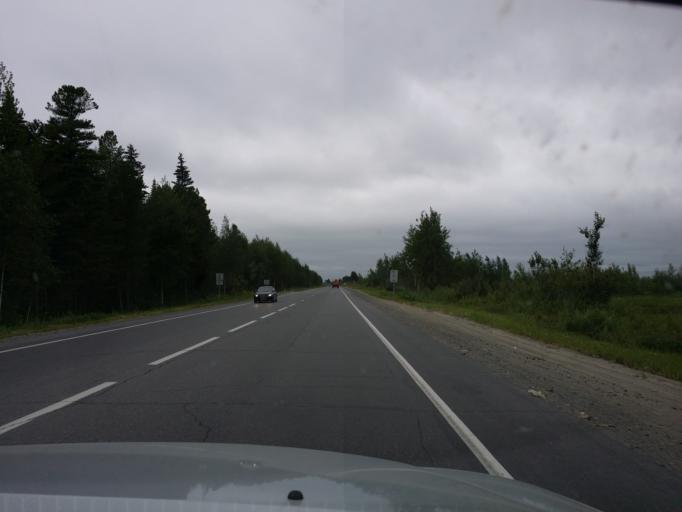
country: RU
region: Khanty-Mansiyskiy Avtonomnyy Okrug
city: Megion
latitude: 61.0652
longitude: 76.2639
